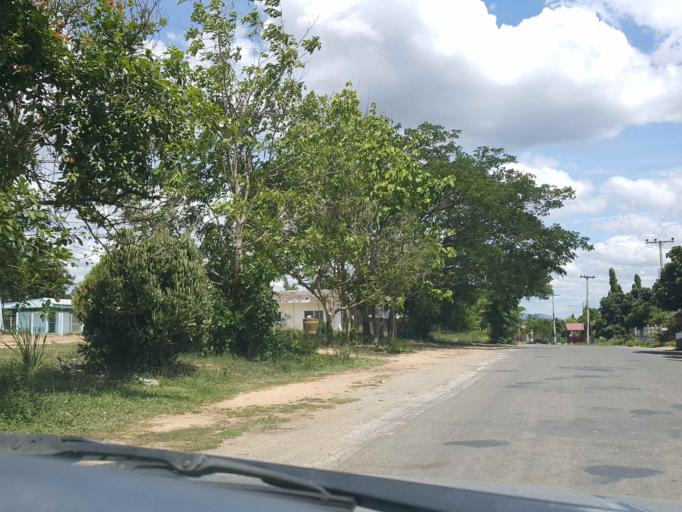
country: TH
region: Chiang Mai
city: Doi Lo
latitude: 18.4681
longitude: 98.7600
